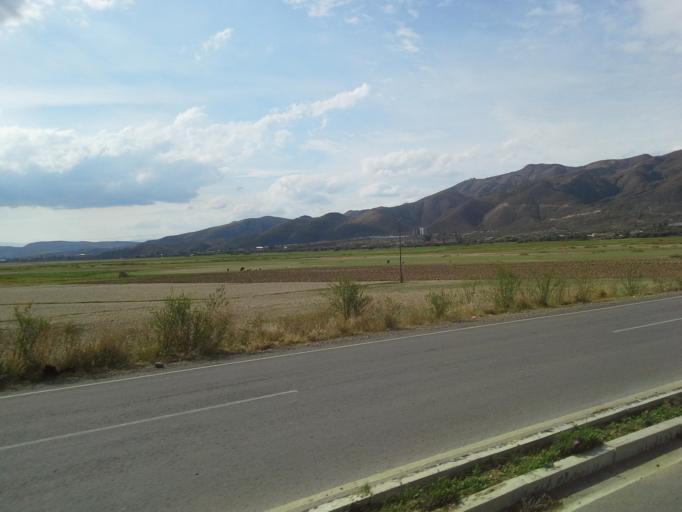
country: BO
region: Cochabamba
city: Tarata
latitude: -17.5570
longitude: -66.0080
